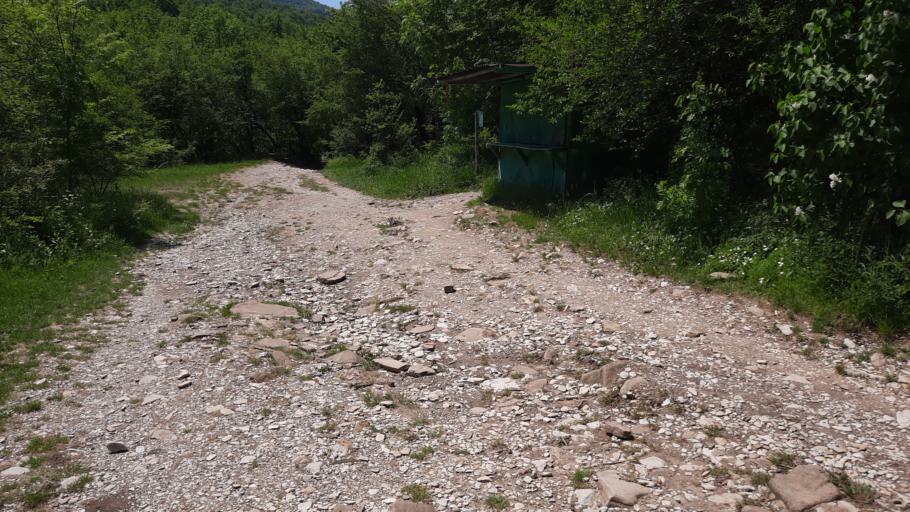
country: RU
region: Krasnodarskiy
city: Divnomorskoye
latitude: 44.5508
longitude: 38.2478
